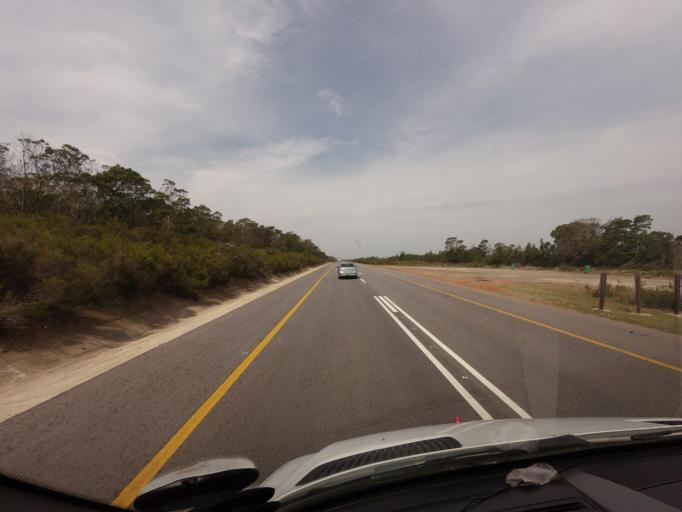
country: ZA
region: Eastern Cape
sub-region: Cacadu District Municipality
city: Kruisfontein
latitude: -33.9956
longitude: 24.7125
